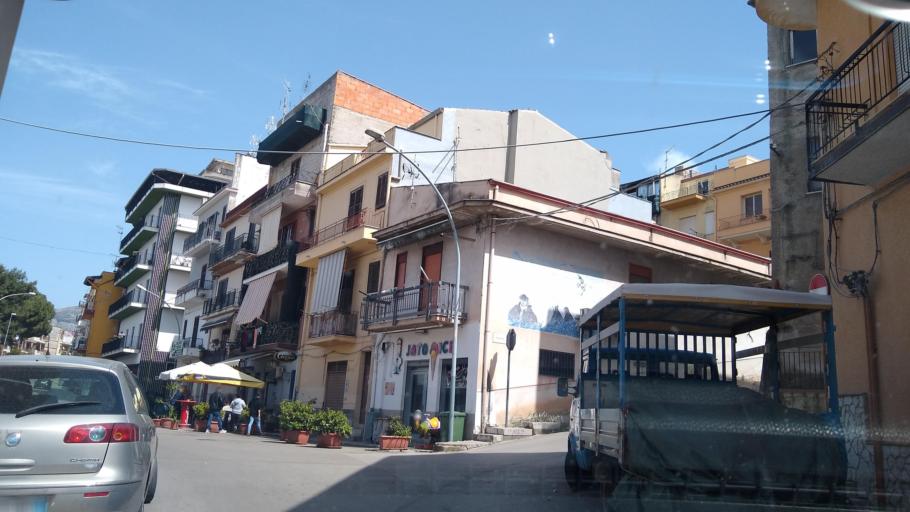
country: IT
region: Sicily
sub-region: Palermo
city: San Giuseppe Jato
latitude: 37.9725
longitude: 13.1865
